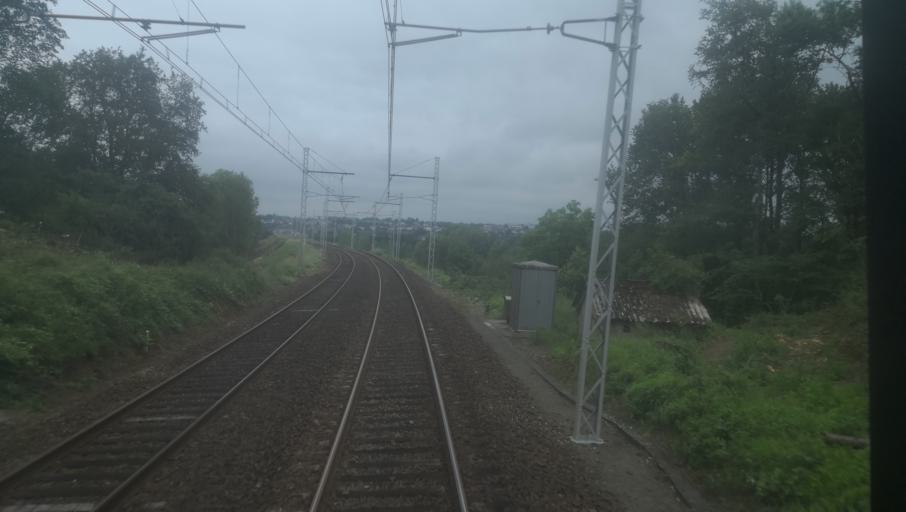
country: FR
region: Centre
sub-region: Departement de l'Indre
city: Argenton-sur-Creuse
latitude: 46.5737
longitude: 1.5274
